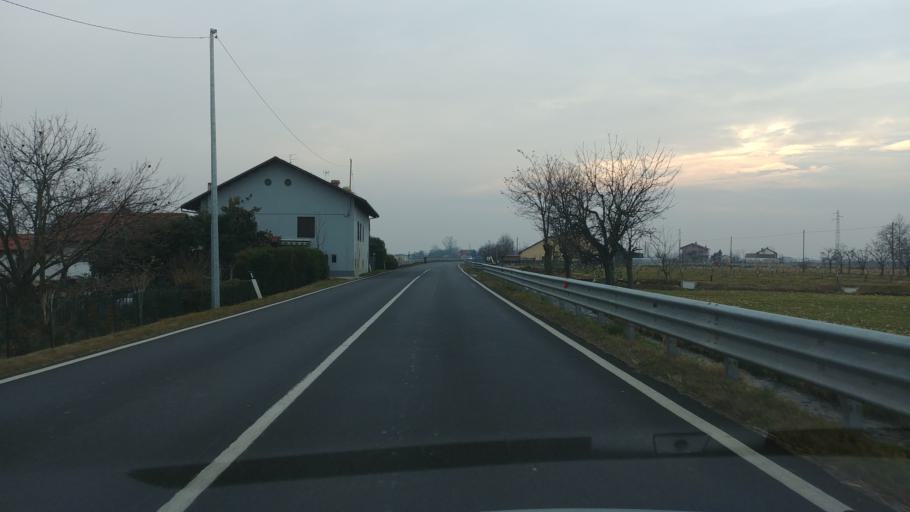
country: IT
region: Piedmont
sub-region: Provincia di Cuneo
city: Montanera
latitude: 44.4751
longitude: 7.6424
